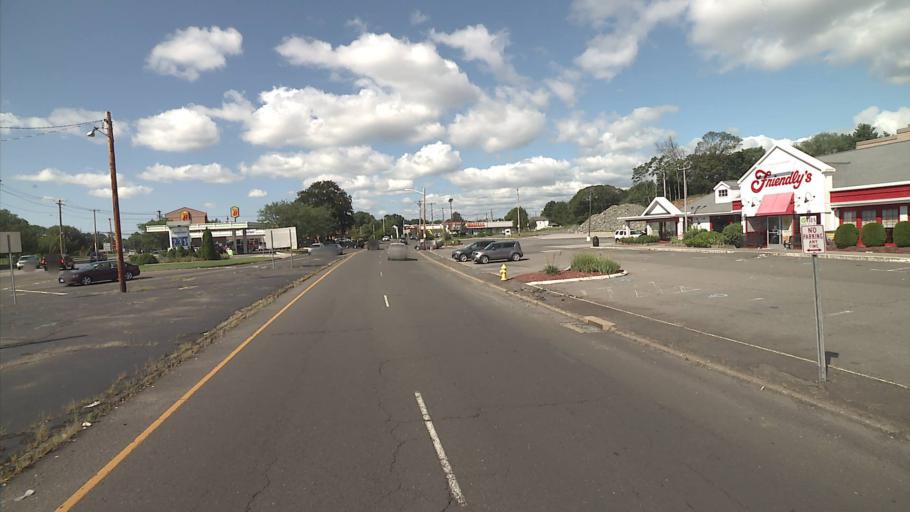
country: US
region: Connecticut
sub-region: New Haven County
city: Milford
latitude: 41.2324
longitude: -73.0448
